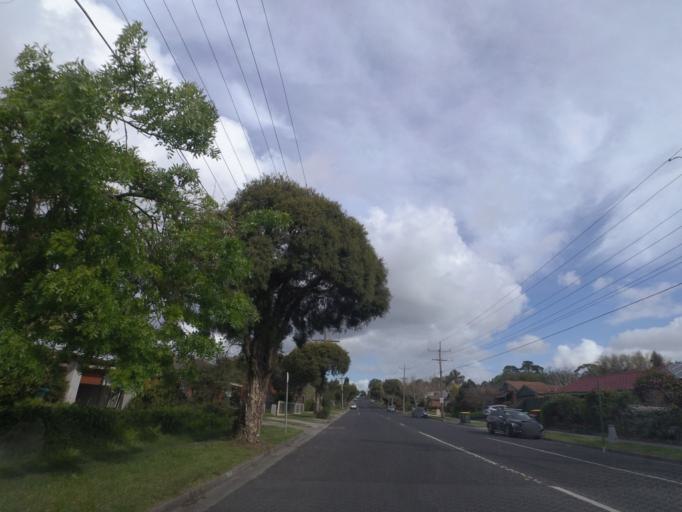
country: AU
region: Victoria
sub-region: Knox
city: Wantirna
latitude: -37.8327
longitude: 145.2134
